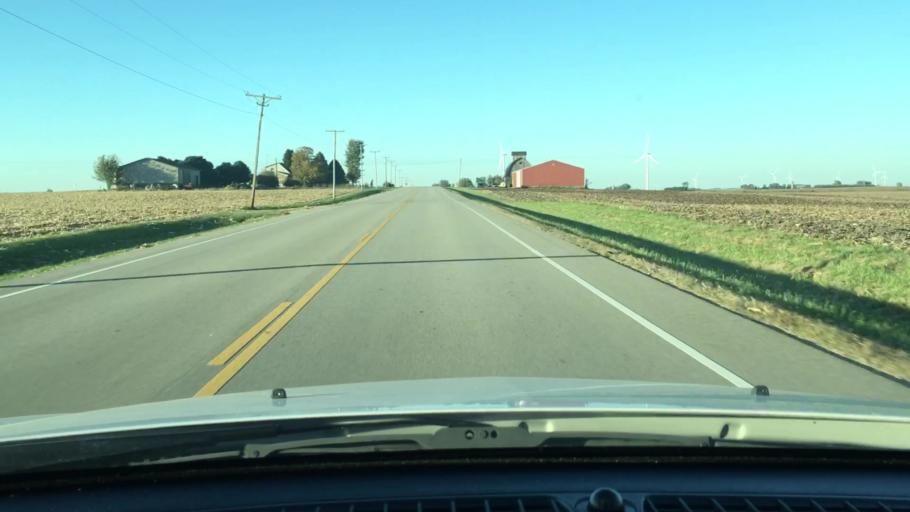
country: US
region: Illinois
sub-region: DeKalb County
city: Malta
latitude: 41.8275
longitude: -88.8864
